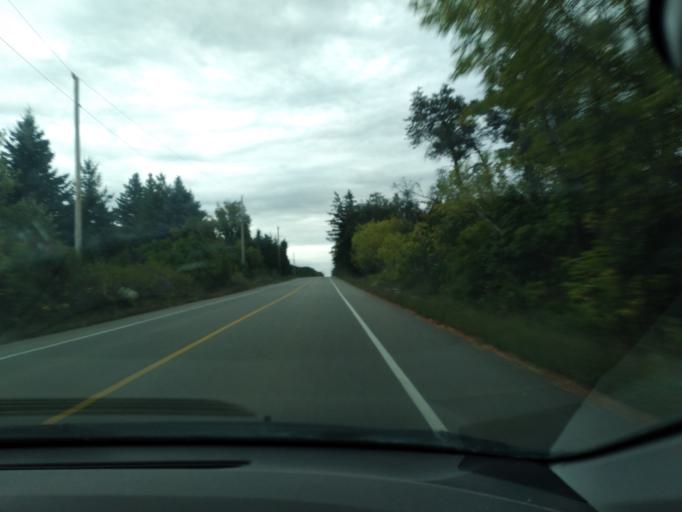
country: CA
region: Ontario
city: Bradford West Gwillimbury
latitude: 43.9700
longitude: -79.7910
